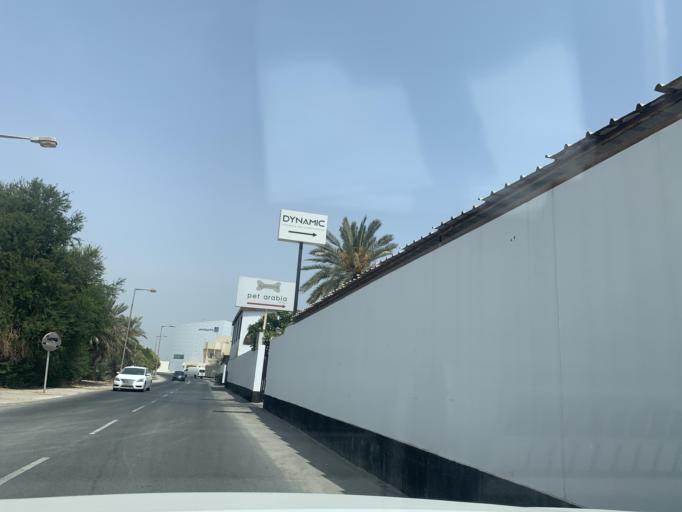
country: BH
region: Manama
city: Jidd Hafs
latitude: 26.2187
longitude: 50.5013
